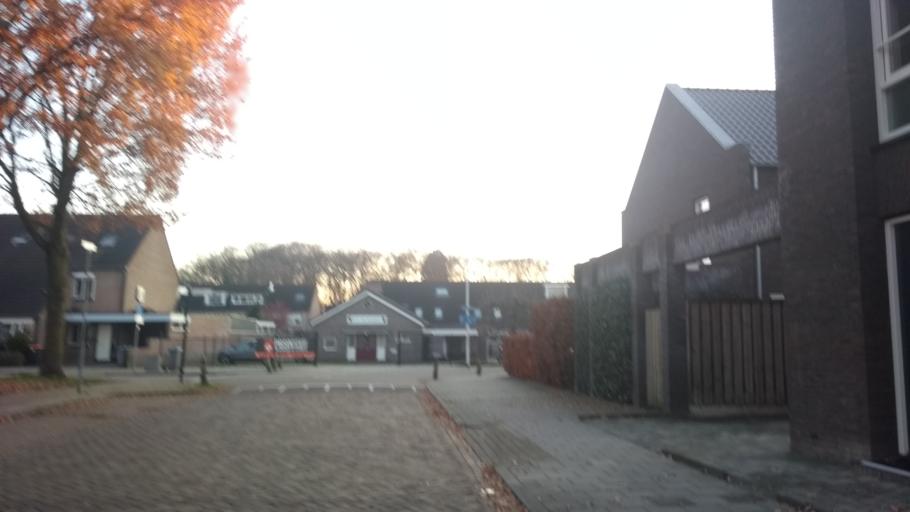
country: NL
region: Overijssel
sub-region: Gemeente Almelo
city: Almelo
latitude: 52.3608
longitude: 6.6707
